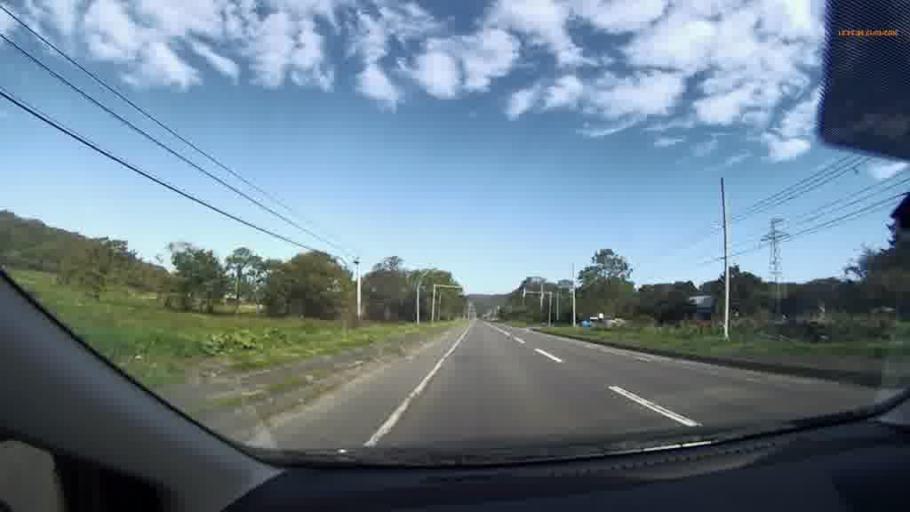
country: JP
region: Hokkaido
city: Kushiro
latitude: 42.9776
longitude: 144.0658
